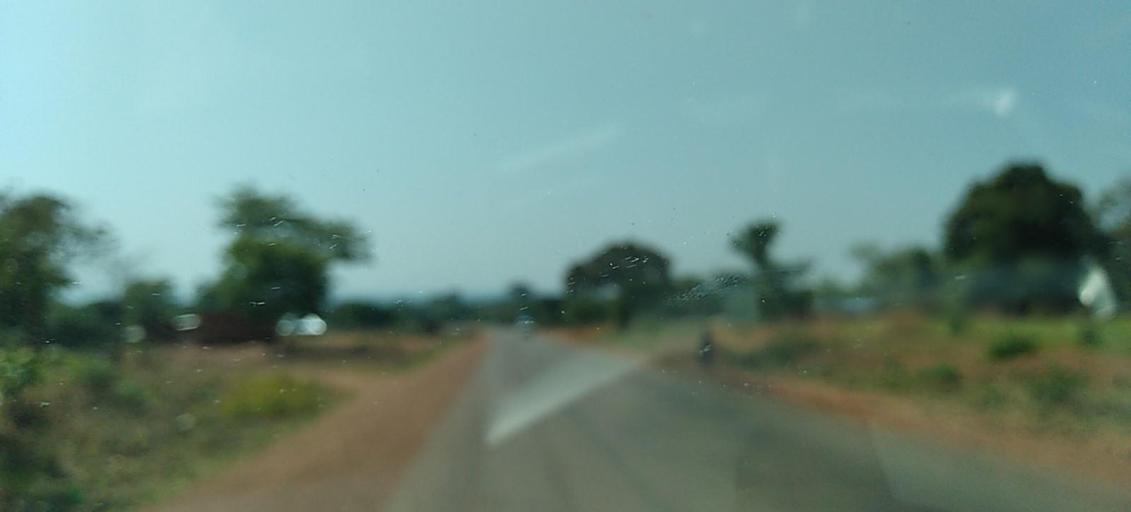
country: ZM
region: North-Western
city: Solwezi
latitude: -12.1151
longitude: 25.5069
